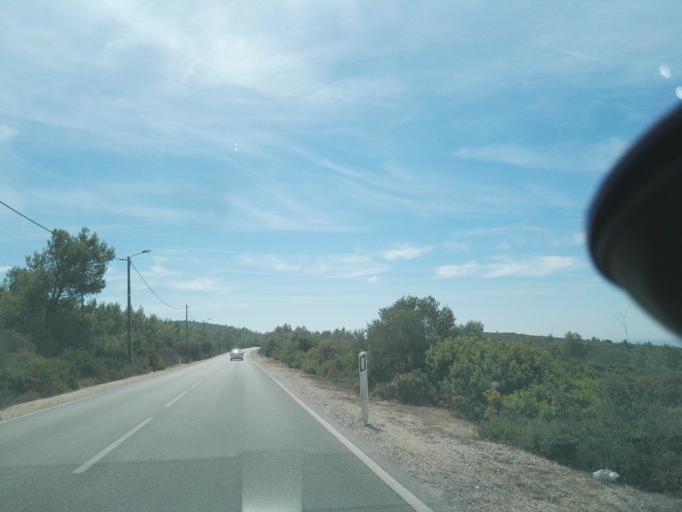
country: PT
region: Setubal
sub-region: Sesimbra
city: Sesimbra
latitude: 38.4543
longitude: -9.0916
